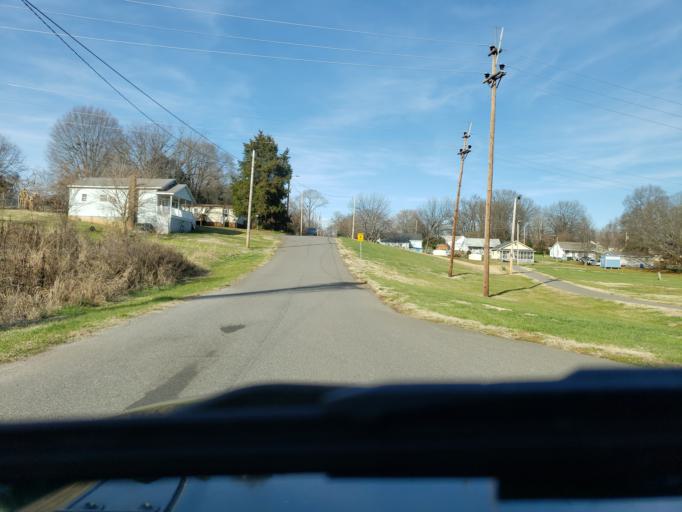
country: US
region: North Carolina
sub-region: Cleveland County
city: Kings Mountain
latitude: 35.2451
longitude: -81.3347
